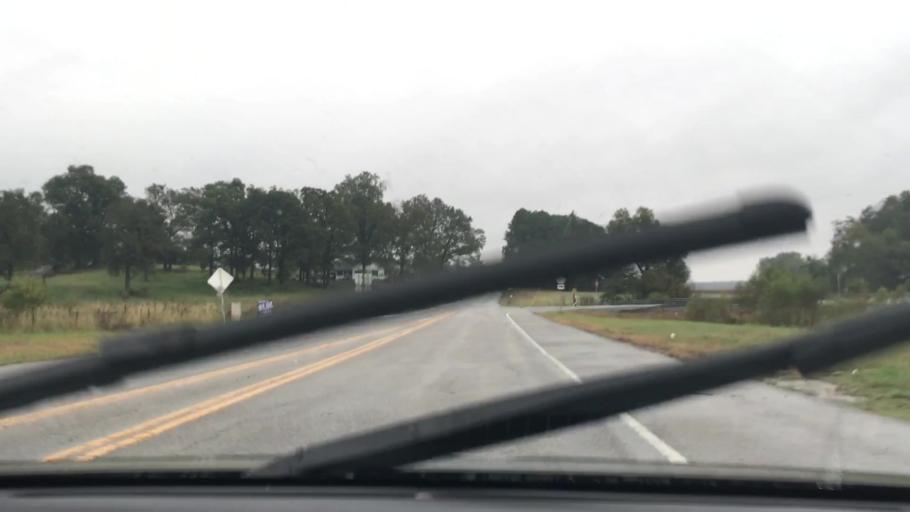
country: US
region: Kentucky
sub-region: Webster County
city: Sebree
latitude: 37.4898
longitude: -87.4725
